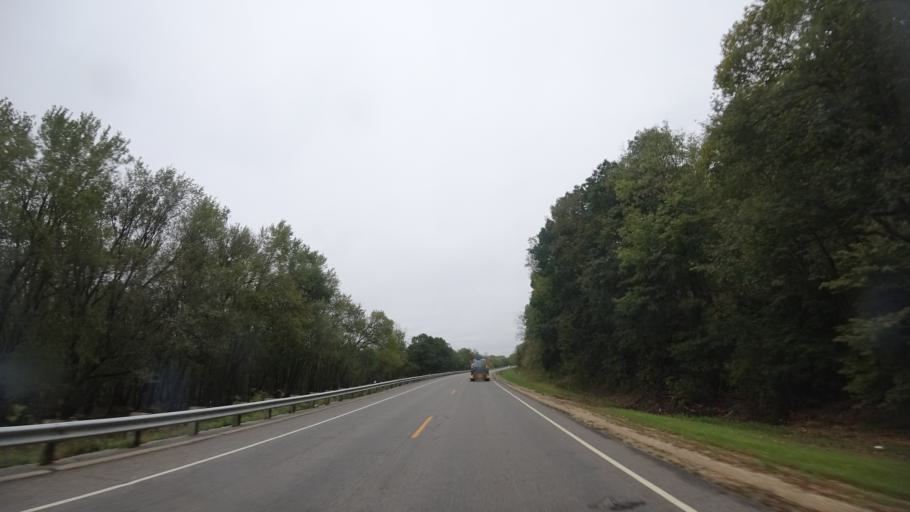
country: US
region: Wisconsin
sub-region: Crawford County
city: Prairie du Chien
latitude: 43.0654
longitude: -90.9499
